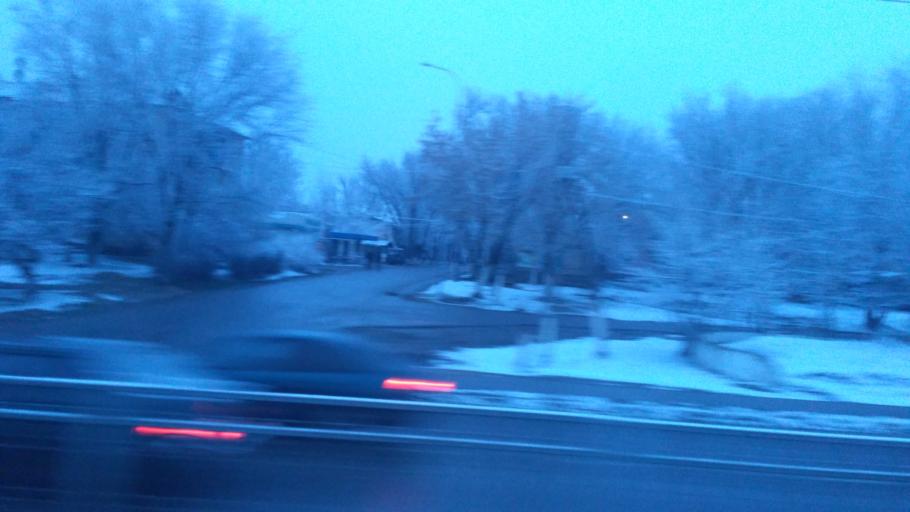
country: KZ
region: Ongtustik Qazaqstan
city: Shymkent
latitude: 42.3797
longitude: 69.4943
